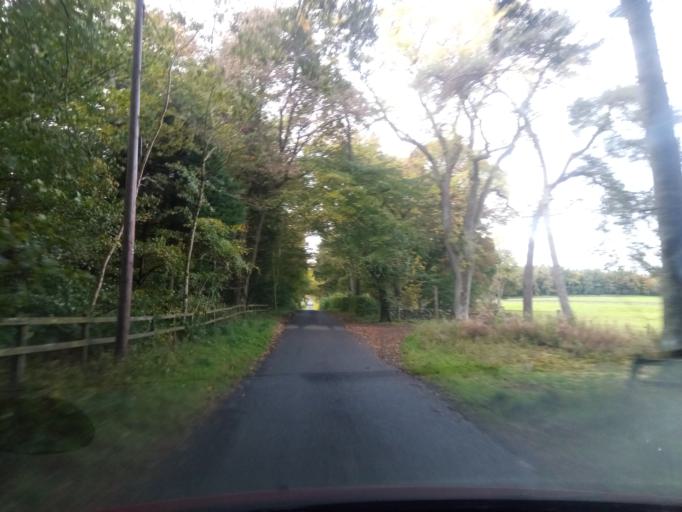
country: GB
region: Scotland
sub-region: The Scottish Borders
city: Galashiels
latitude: 55.6692
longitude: -2.8169
